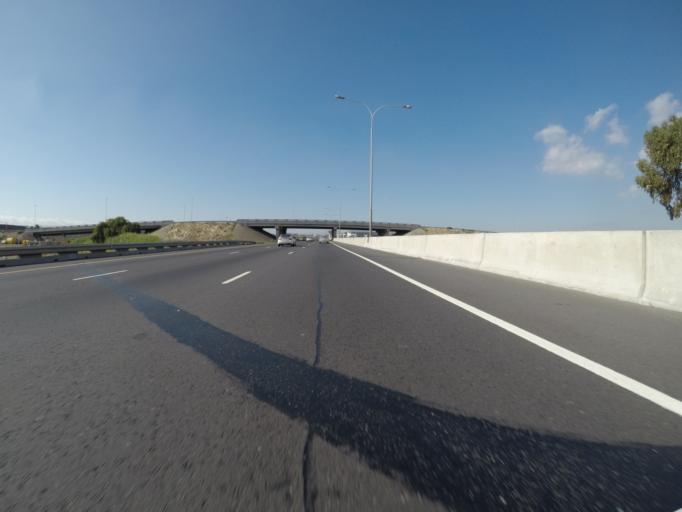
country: ZA
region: Western Cape
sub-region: City of Cape Town
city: Kraaifontein
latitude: -33.9086
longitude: 18.6718
